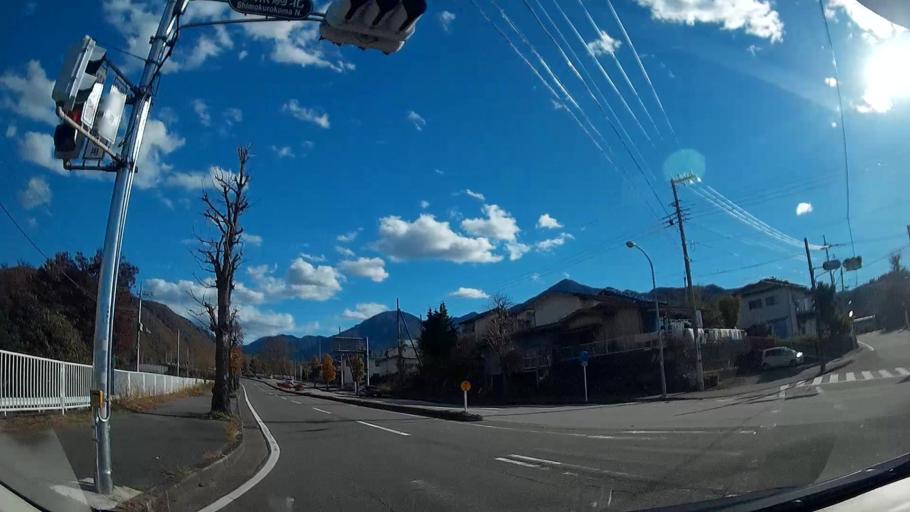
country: JP
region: Yamanashi
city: Isawa
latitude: 35.6222
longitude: 138.6894
